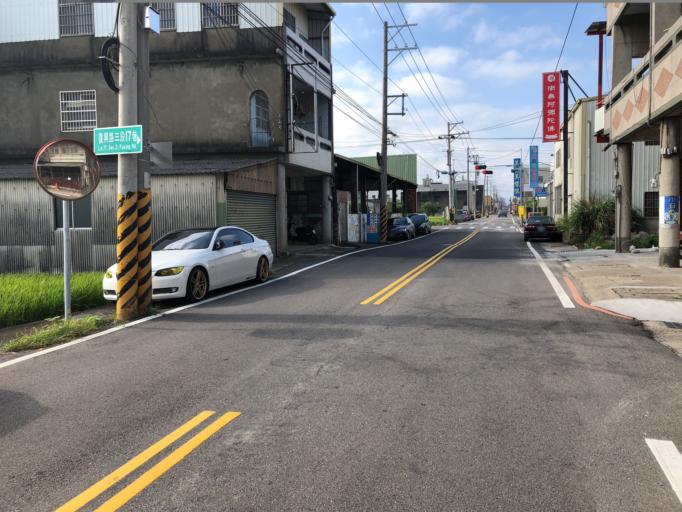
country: TW
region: Taiwan
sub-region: Miaoli
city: Miaoli
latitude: 24.5595
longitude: 120.8280
